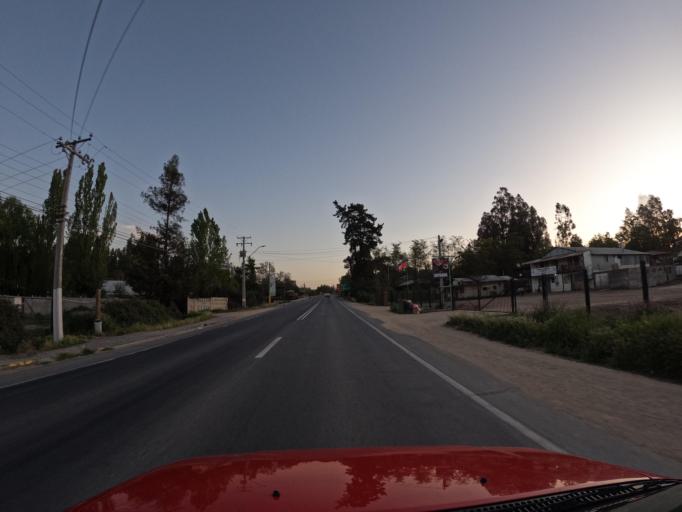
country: CL
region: O'Higgins
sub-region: Provincia de Cachapoal
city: San Vicente
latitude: -34.1758
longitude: -71.3981
